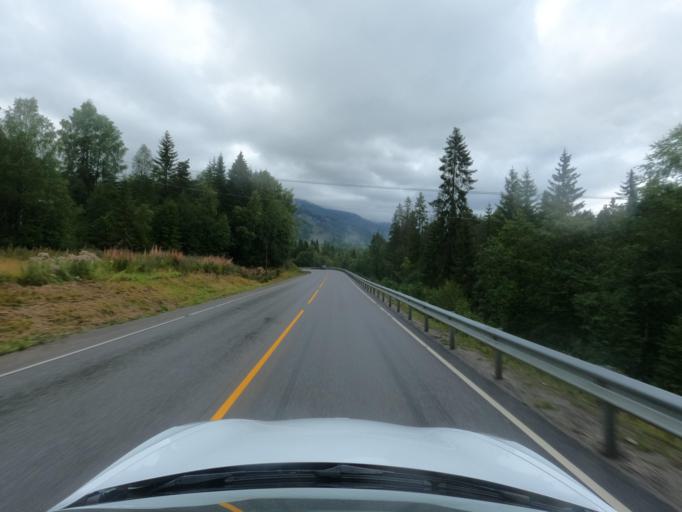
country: NO
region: Telemark
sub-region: Seljord
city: Seljord
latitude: 59.4493
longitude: 8.5630
